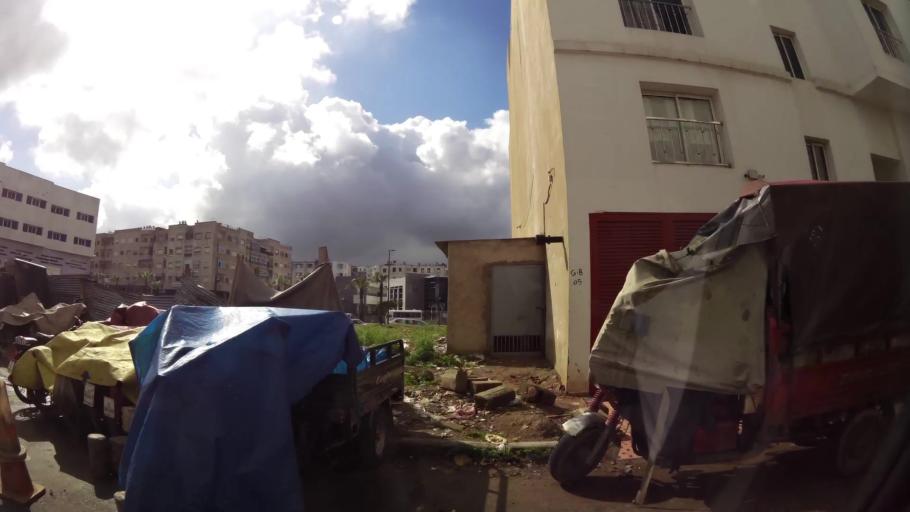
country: MA
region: Grand Casablanca
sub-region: Mediouna
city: Tit Mellil
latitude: 33.5751
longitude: -7.5225
